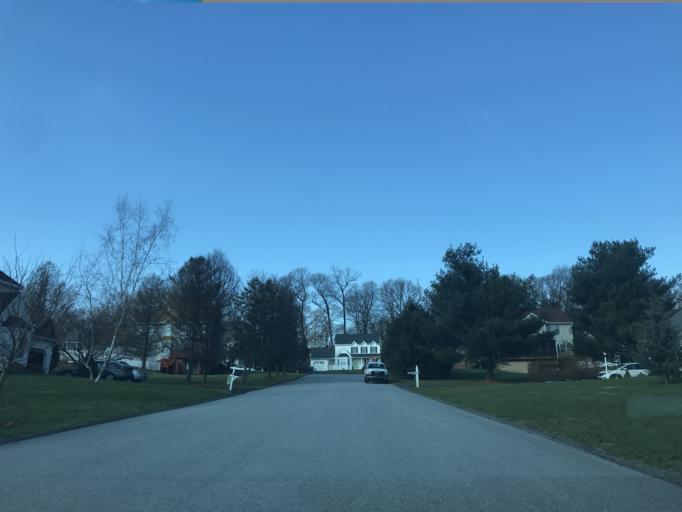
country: US
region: Pennsylvania
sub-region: York County
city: New Freedom
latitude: 39.7336
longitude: -76.6875
